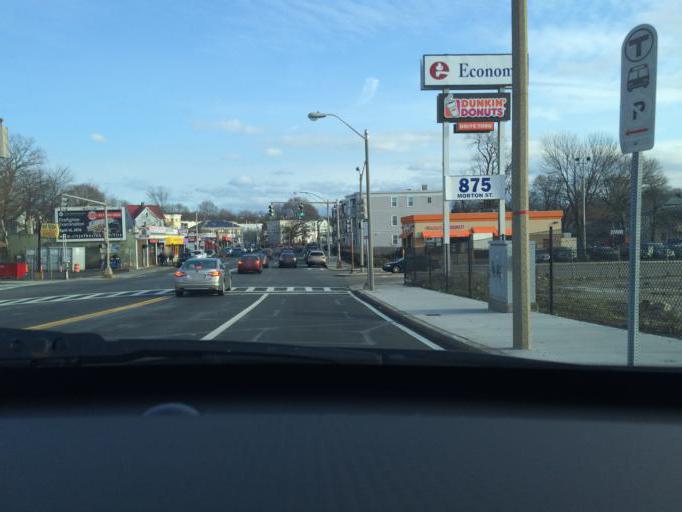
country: US
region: Massachusetts
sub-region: Norfolk County
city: Milton
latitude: 42.2809
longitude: -71.0850
